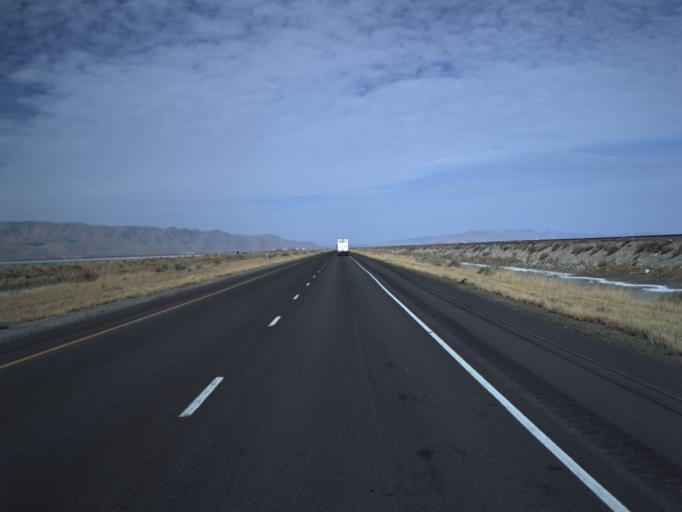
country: US
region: Utah
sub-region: Tooele County
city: Stansbury park
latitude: 40.6698
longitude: -112.3811
